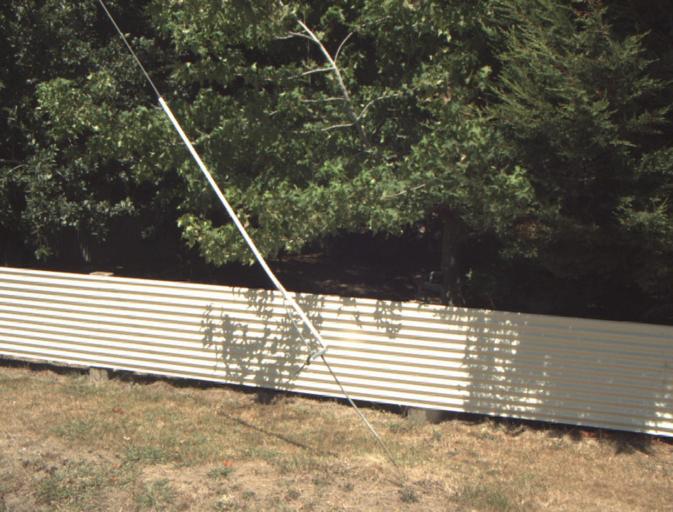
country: AU
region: Tasmania
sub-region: Launceston
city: Mayfield
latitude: -41.2656
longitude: 147.1345
